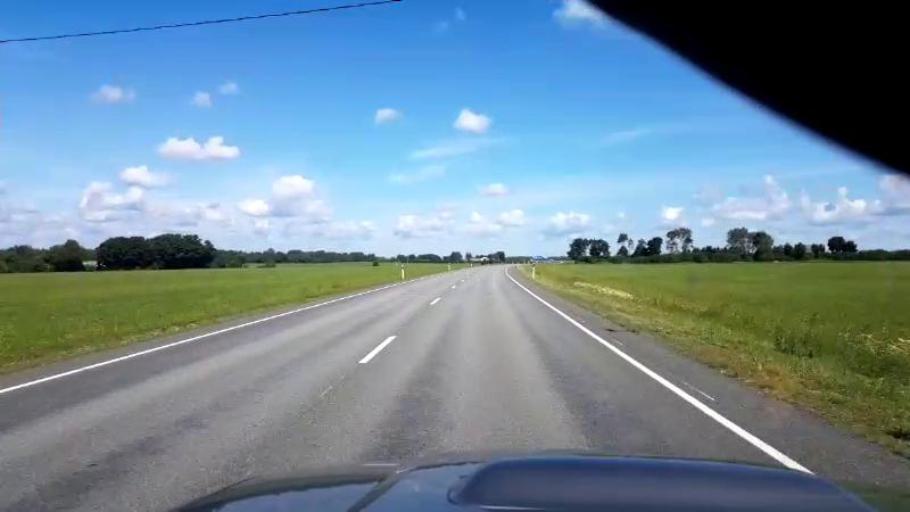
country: EE
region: Jaervamaa
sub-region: Jaerva-Jaani vald
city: Jarva-Jaani
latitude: 59.1661
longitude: 25.7590
